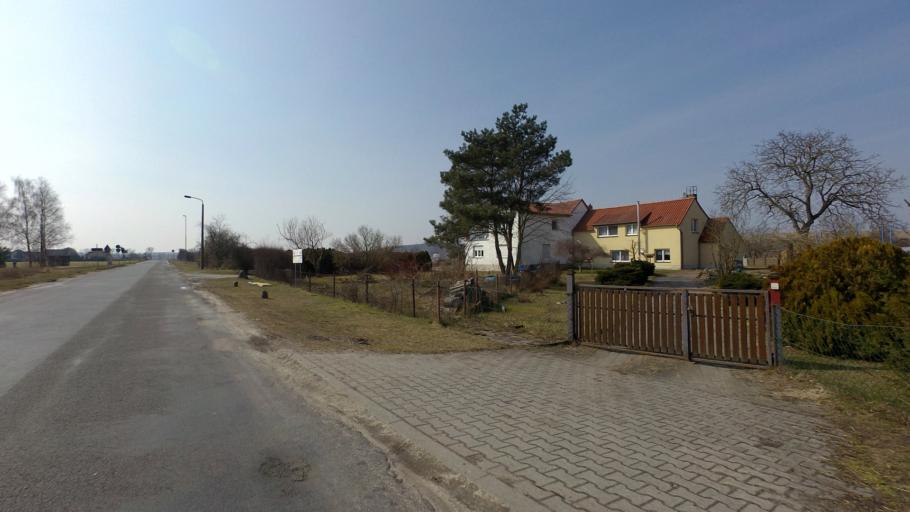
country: DE
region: Brandenburg
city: Ketzin
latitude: 52.4515
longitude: 12.8064
